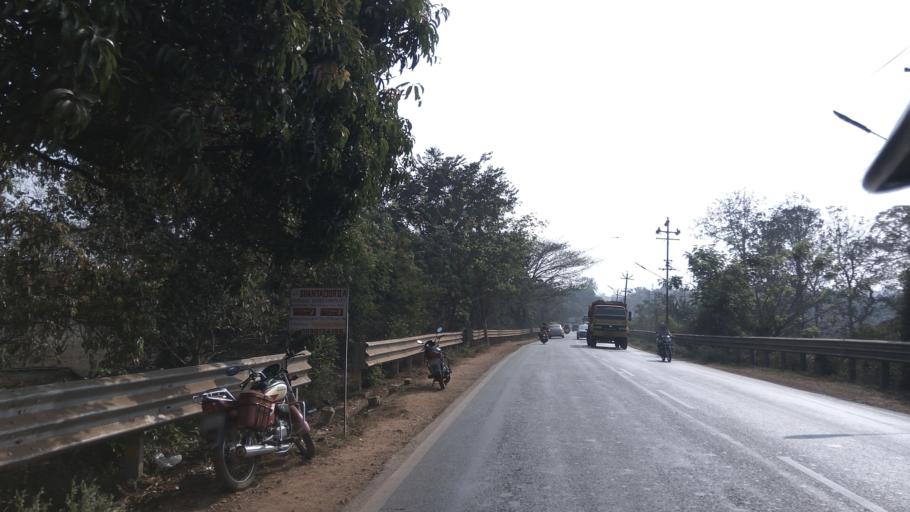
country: IN
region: Goa
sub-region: North Goa
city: Jua
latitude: 15.4975
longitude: 73.9254
